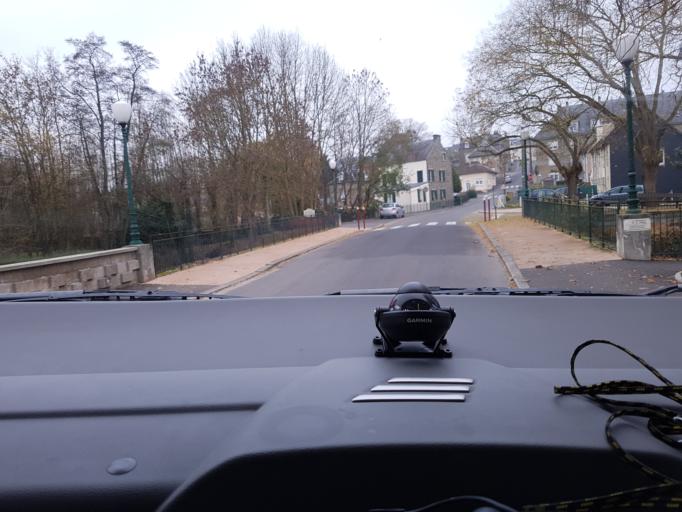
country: FR
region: Lower Normandy
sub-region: Departement du Calvados
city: Conde-sur-Noireau
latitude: 48.8512
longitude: -0.5534
